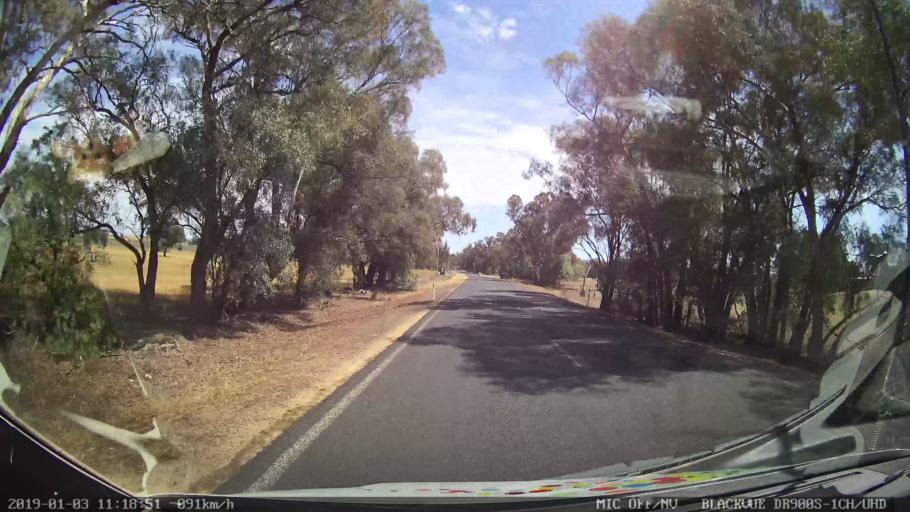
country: AU
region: New South Wales
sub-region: Young
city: Young
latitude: -34.1206
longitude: 148.2608
